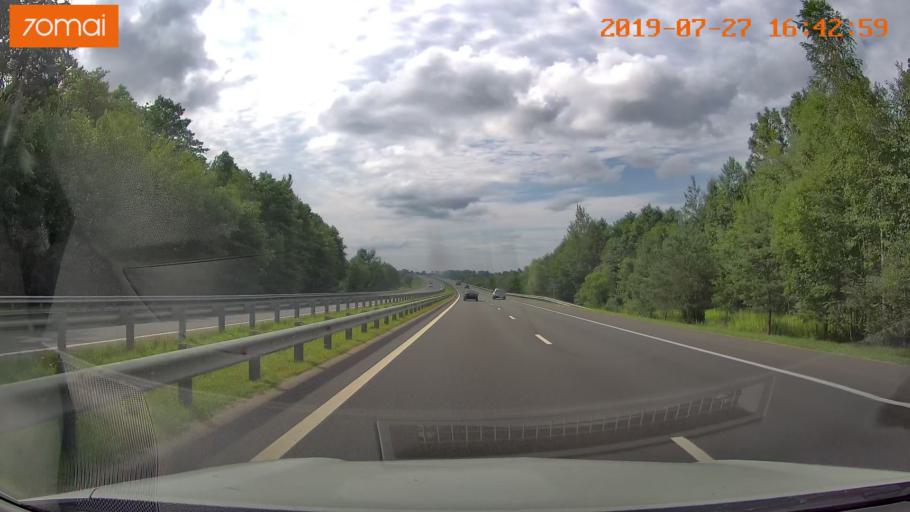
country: RU
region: Kaliningrad
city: Gvardeysk
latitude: 54.6686
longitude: 21.1137
